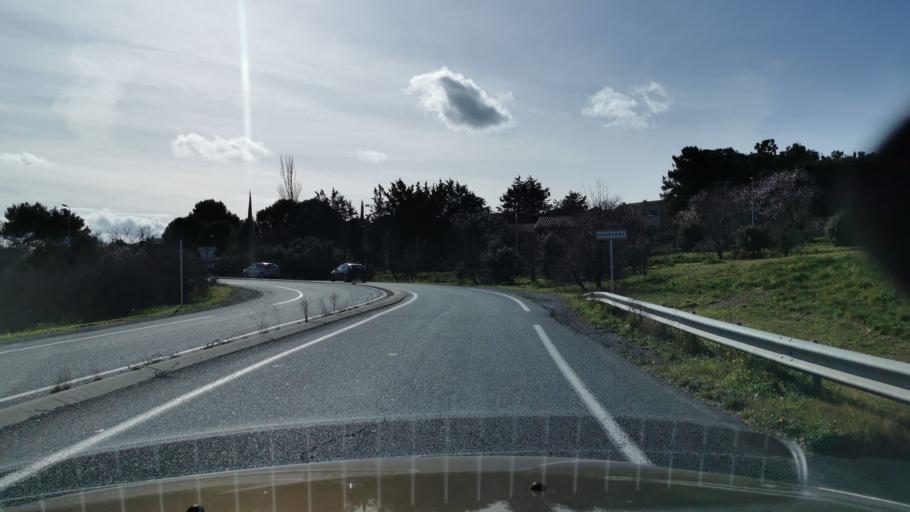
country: FR
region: Languedoc-Roussillon
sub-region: Departement de l'Aude
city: Narbonne
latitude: 43.1684
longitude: 2.9818
